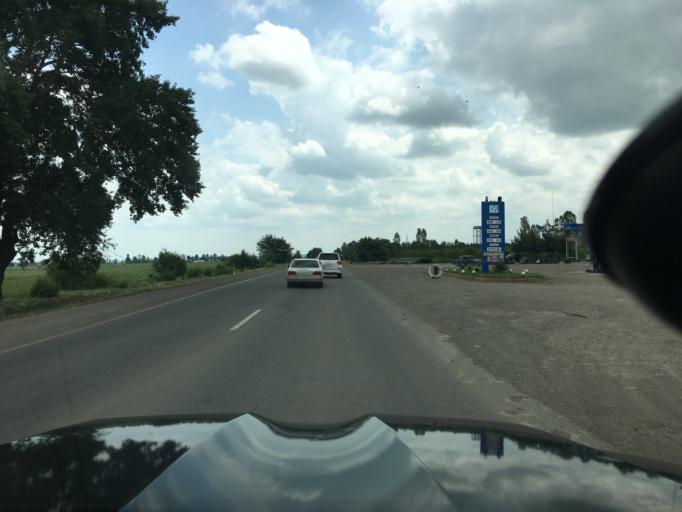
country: AZ
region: Tovuz
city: Tovuz
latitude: 40.9624
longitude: 45.7150
